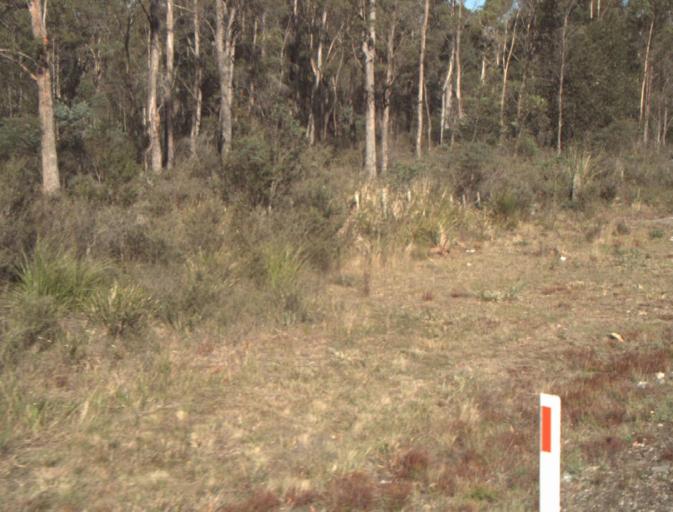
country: AU
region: Tasmania
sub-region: Launceston
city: Mayfield
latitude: -41.3322
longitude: 147.1793
